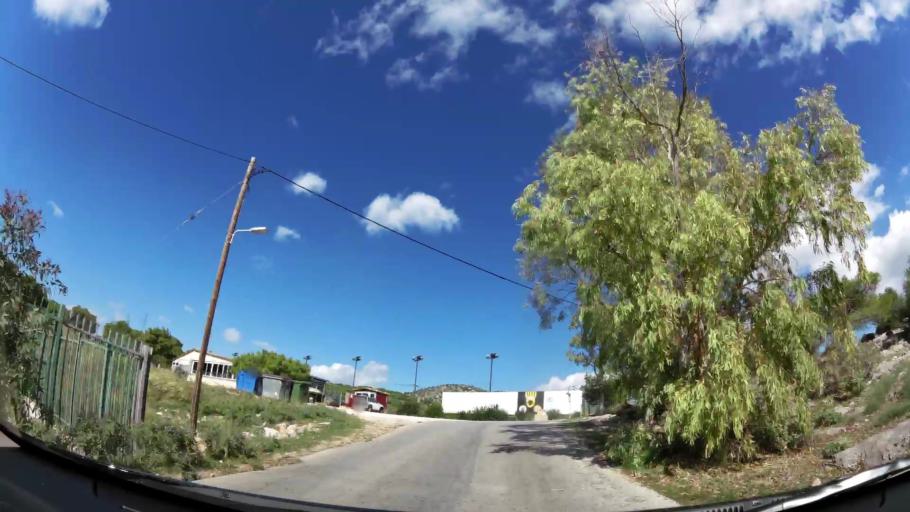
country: GR
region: Attica
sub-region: Nomarchia Anatolikis Attikis
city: Vari
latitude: 37.8378
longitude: 23.7950
